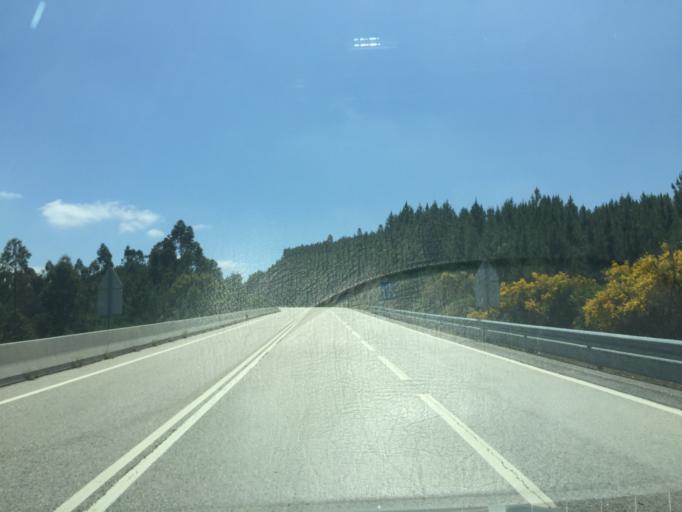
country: PT
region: Castelo Branco
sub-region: Vila de Rei
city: Vila de Rei
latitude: 39.7121
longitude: -8.1415
